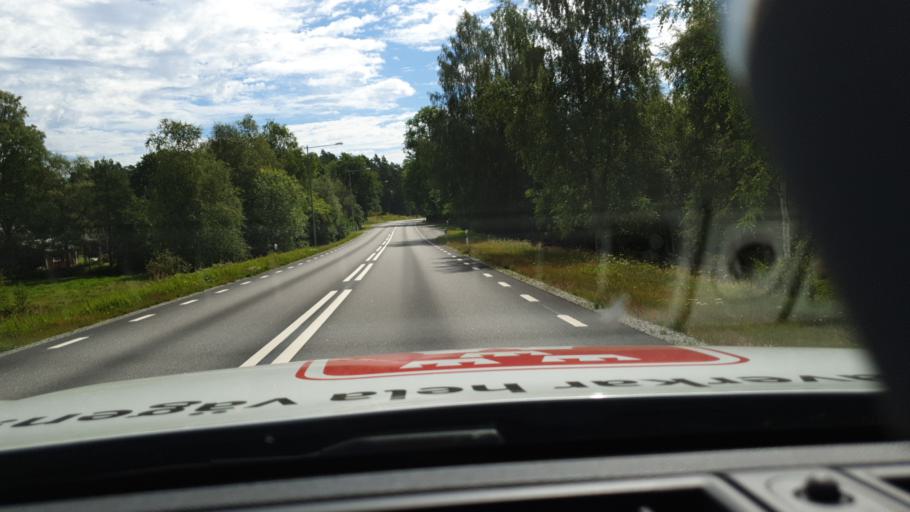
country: SE
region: Joenkoeping
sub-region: Savsjo Kommun
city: Vrigstad
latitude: 57.3093
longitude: 14.5120
